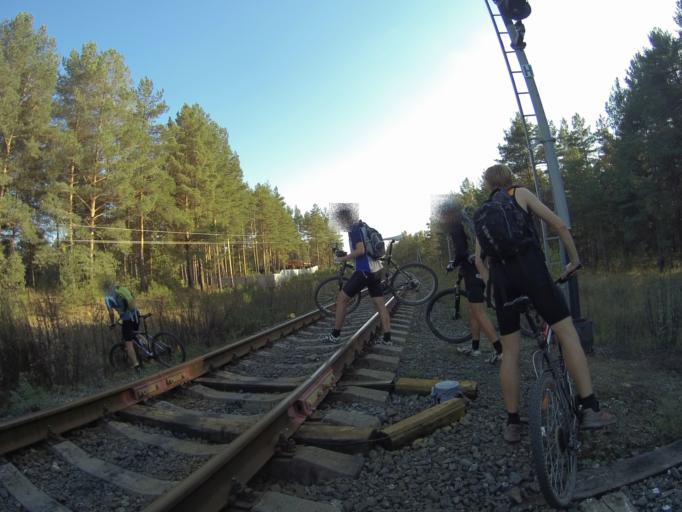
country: RU
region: Vladimir
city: Raduzhnyy
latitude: 56.0344
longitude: 40.3826
